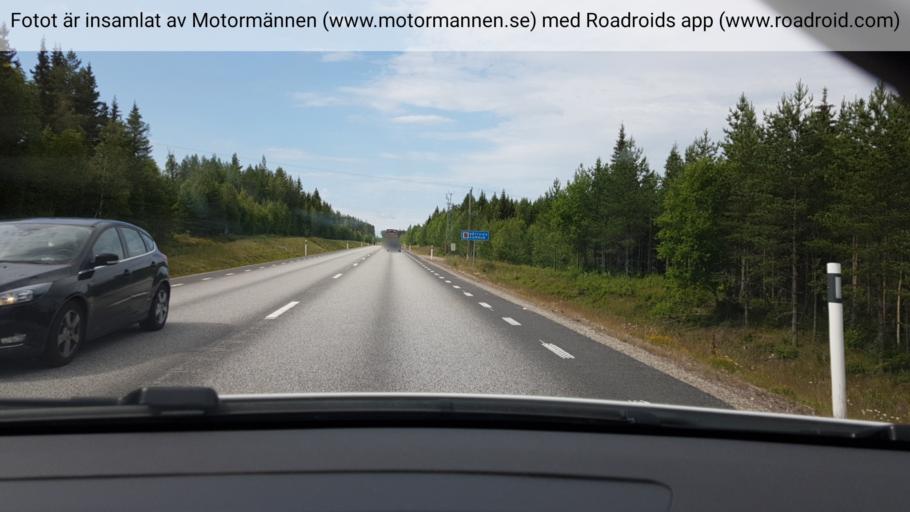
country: SE
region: Dalarna
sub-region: Rattviks Kommun
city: Raettvik
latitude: 60.8227
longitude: 15.2537
